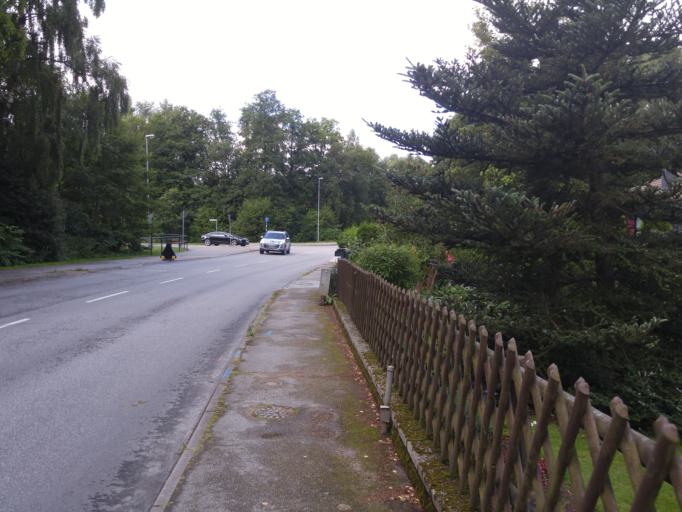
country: SE
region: Skane
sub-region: Hoors Kommun
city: Hoeoer
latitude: 55.9266
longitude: 13.5354
